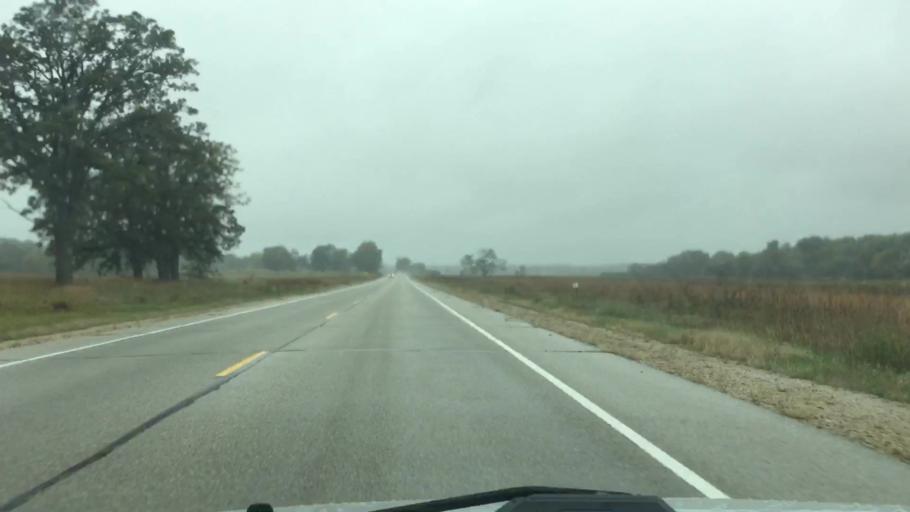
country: US
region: Wisconsin
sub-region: Waukesha County
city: Eagle
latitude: 42.8790
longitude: -88.5191
